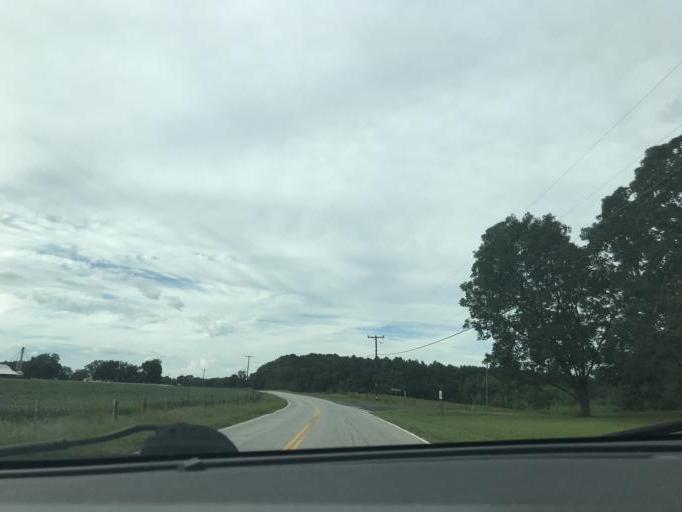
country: US
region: South Carolina
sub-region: Cherokee County
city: East Gaffney
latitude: 35.1155
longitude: -81.6512
